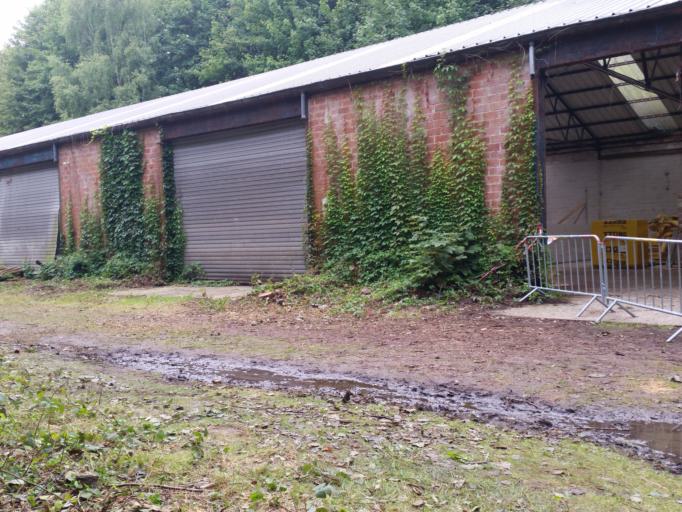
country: BE
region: Flanders
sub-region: Provincie Antwerpen
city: Mechelen
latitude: 51.0610
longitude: 4.4629
